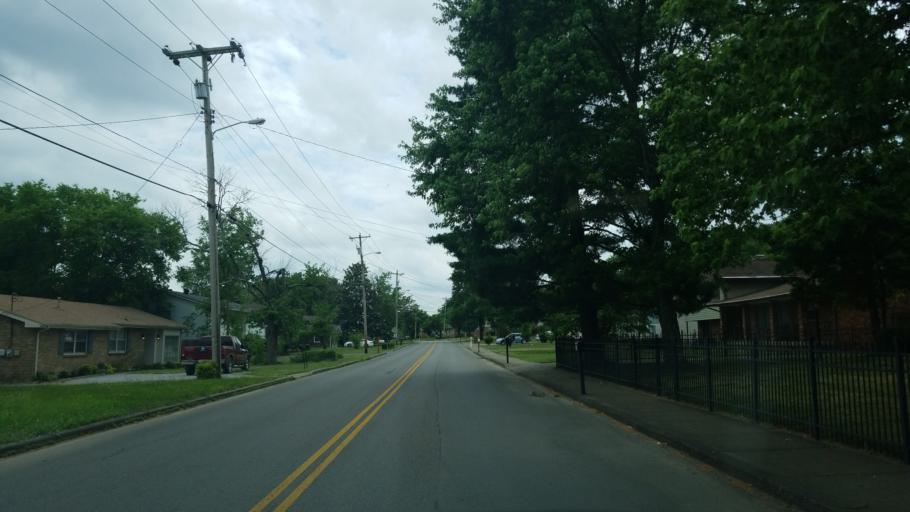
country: US
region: Tennessee
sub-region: Rutherford County
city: La Vergne
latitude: 36.0860
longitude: -86.6230
